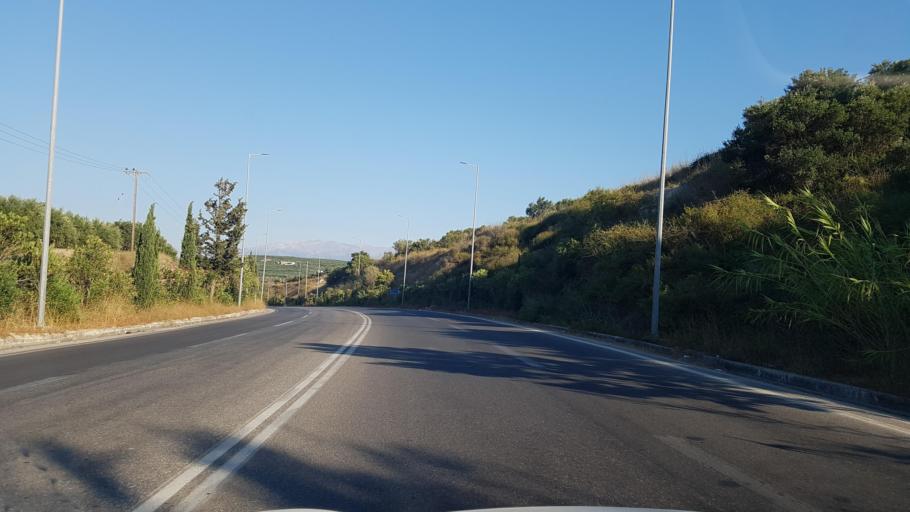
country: GR
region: Crete
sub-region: Nomos Chanias
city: Kolympari
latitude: 35.5314
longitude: 23.7796
